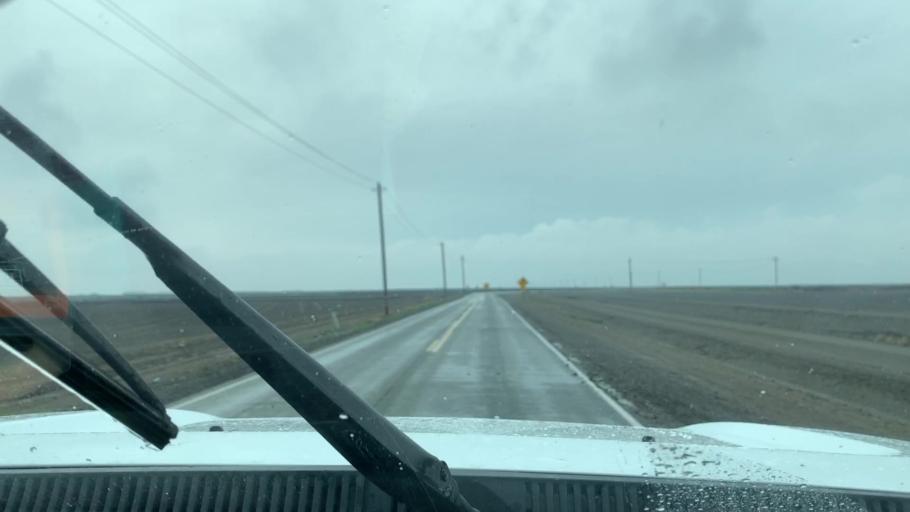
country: US
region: California
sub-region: Tulare County
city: Alpaugh
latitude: 35.9652
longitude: -119.5720
